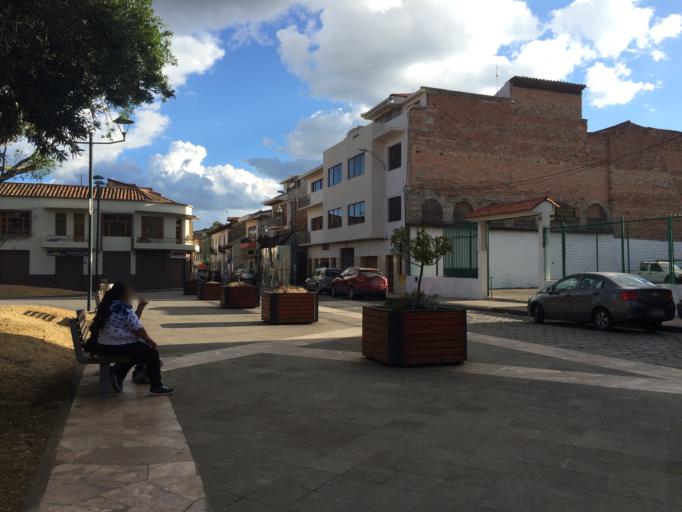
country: EC
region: Azuay
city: Cuenca
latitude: -2.8923
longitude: -79.0060
